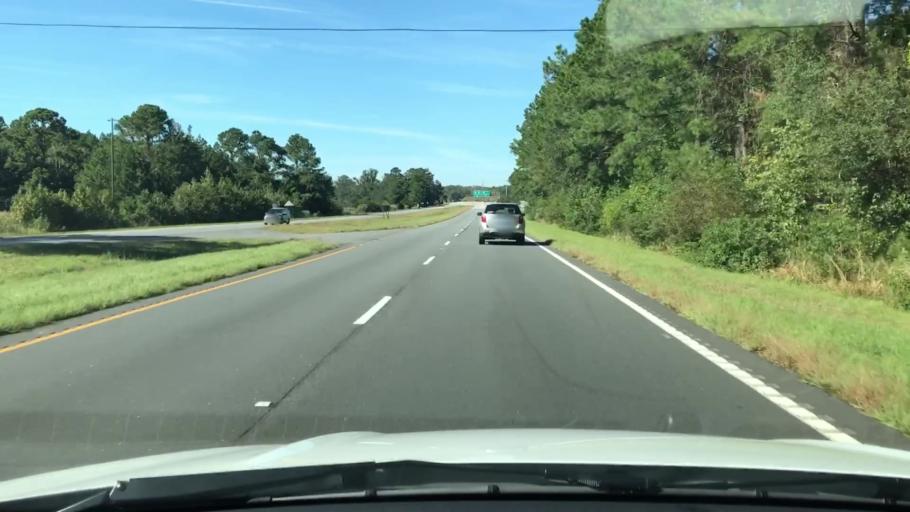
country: US
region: South Carolina
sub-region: Hampton County
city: Yemassee
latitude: 32.5953
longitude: -80.7534
